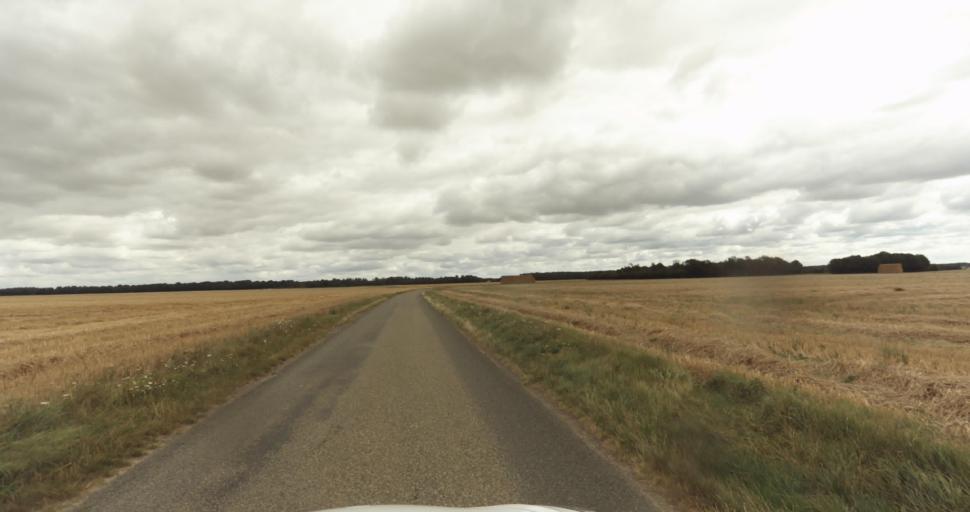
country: FR
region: Haute-Normandie
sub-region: Departement de l'Eure
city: Nonancourt
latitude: 48.8144
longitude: 1.1517
